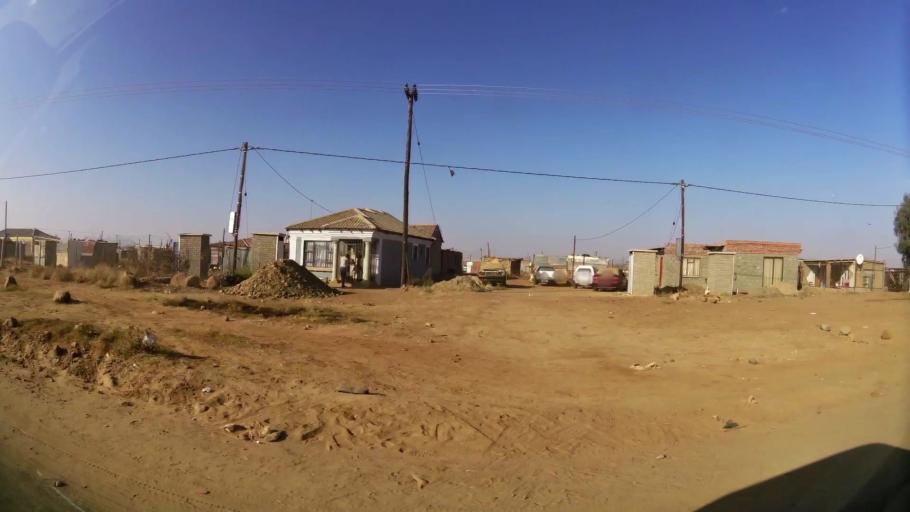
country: ZA
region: Orange Free State
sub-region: Mangaung Metropolitan Municipality
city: Bloemfontein
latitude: -29.2047
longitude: 26.2505
